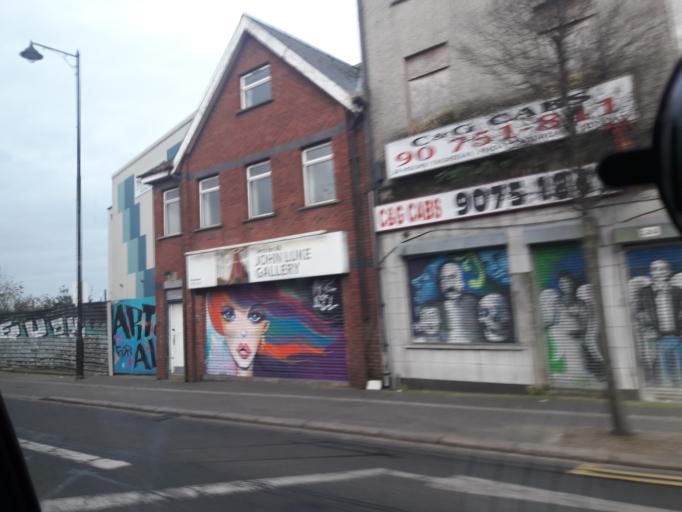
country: GB
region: Northern Ireland
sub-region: City of Belfast
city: Belfast
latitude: 54.6145
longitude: -5.9242
